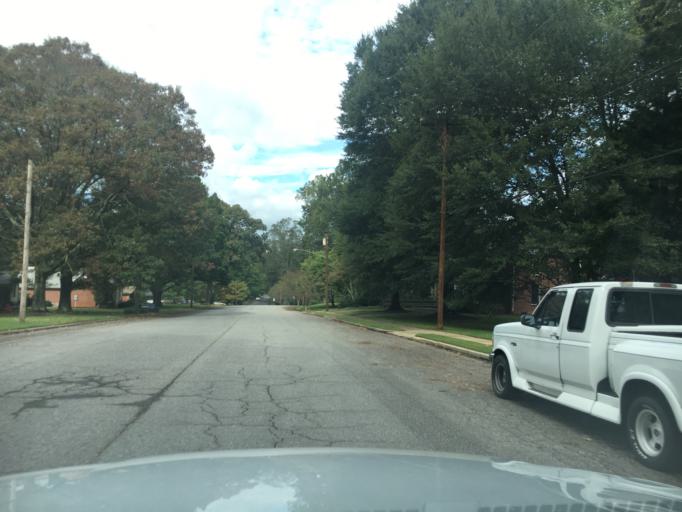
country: US
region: North Carolina
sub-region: Catawba County
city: Hickory
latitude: 35.7365
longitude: -81.3286
